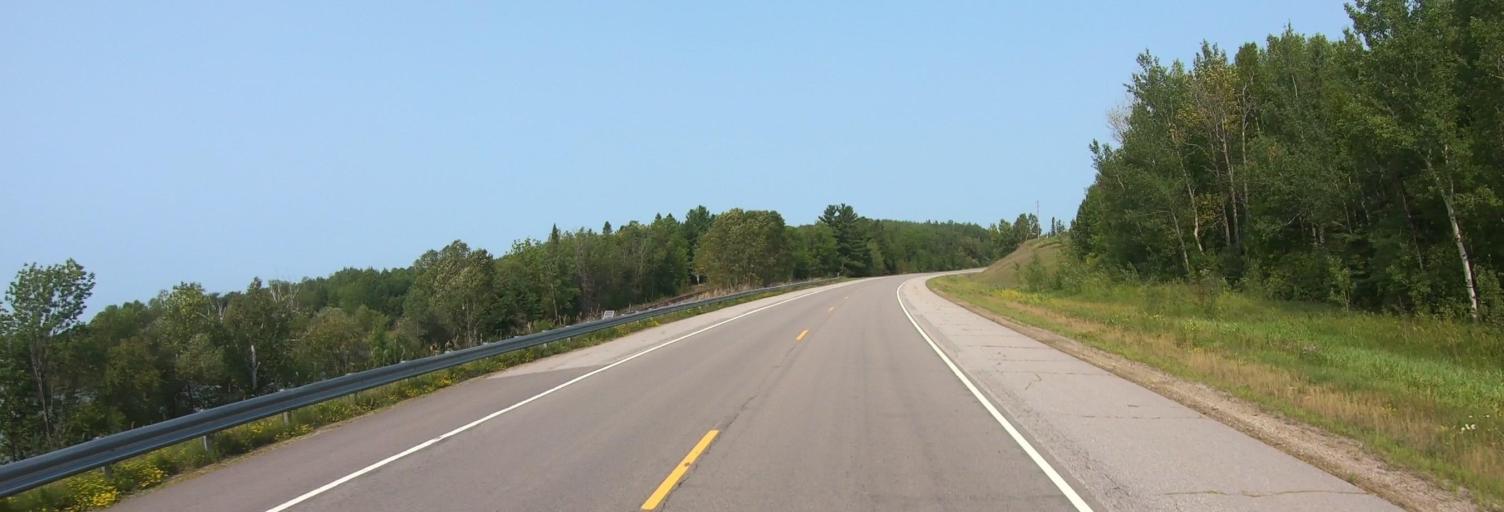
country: CA
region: Ontario
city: Fort Frances
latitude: 48.2204
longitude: -92.9186
